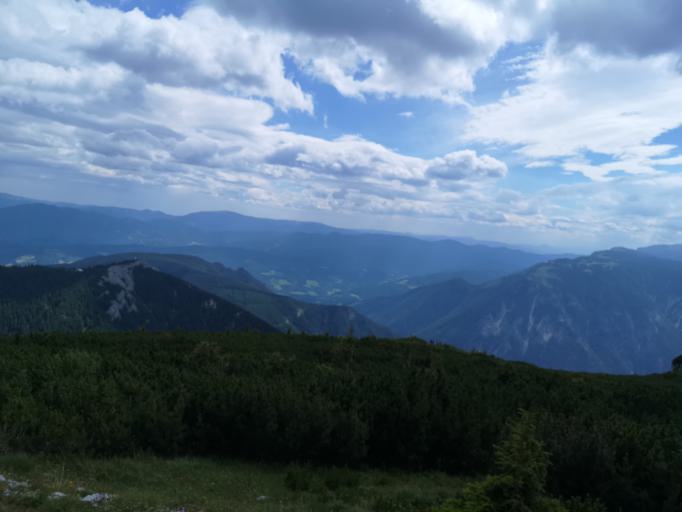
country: AT
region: Lower Austria
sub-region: Politischer Bezirk Neunkirchen
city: Reichenau an der Rax
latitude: 47.7569
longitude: 15.8329
